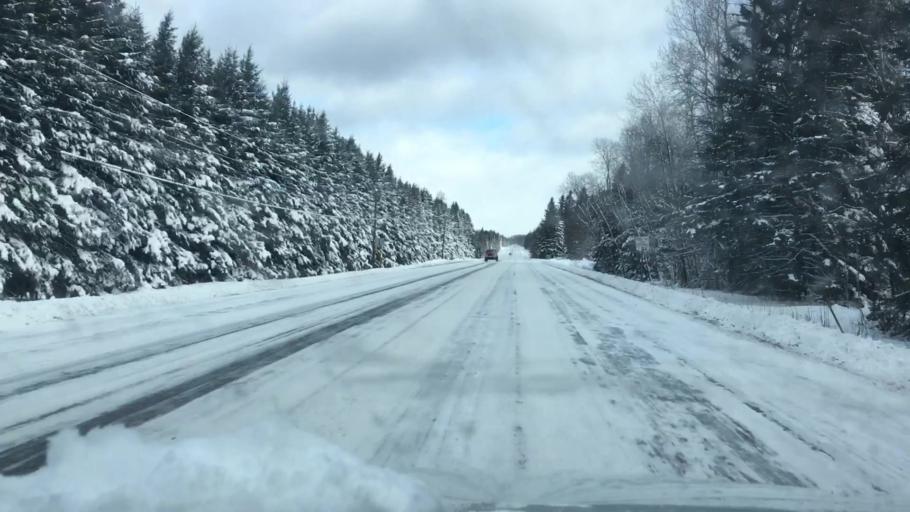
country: US
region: Maine
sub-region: Aroostook County
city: Madawaska
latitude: 47.0175
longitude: -68.0157
